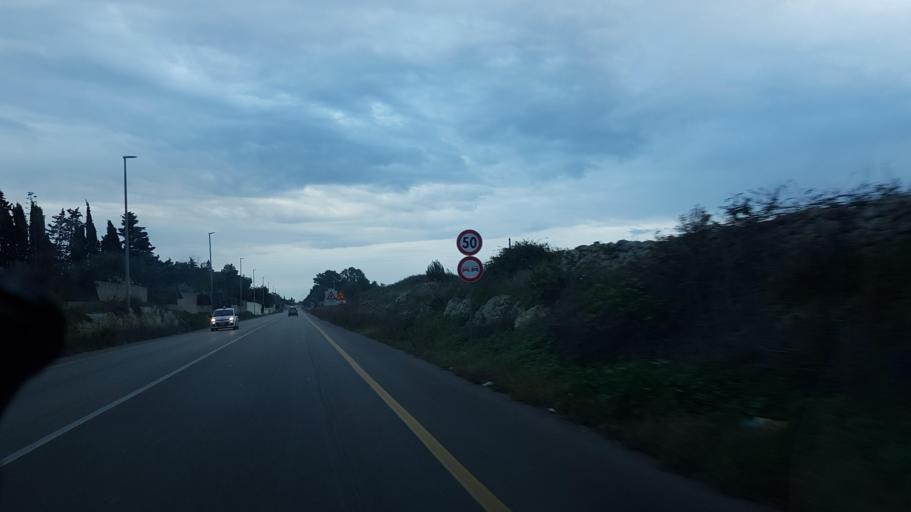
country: IT
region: Apulia
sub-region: Provincia di Lecce
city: Merine
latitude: 40.3426
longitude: 18.2113
